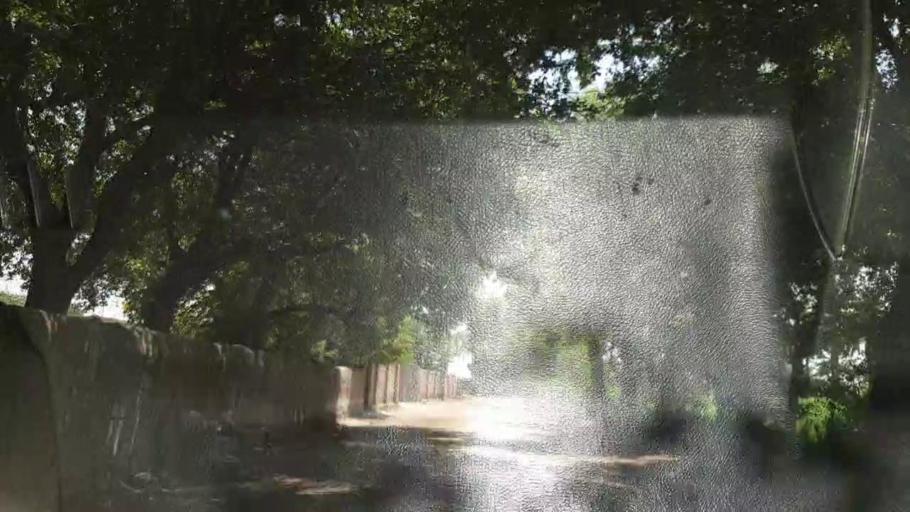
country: PK
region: Sindh
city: Bozdar
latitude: 27.2493
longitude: 68.6858
